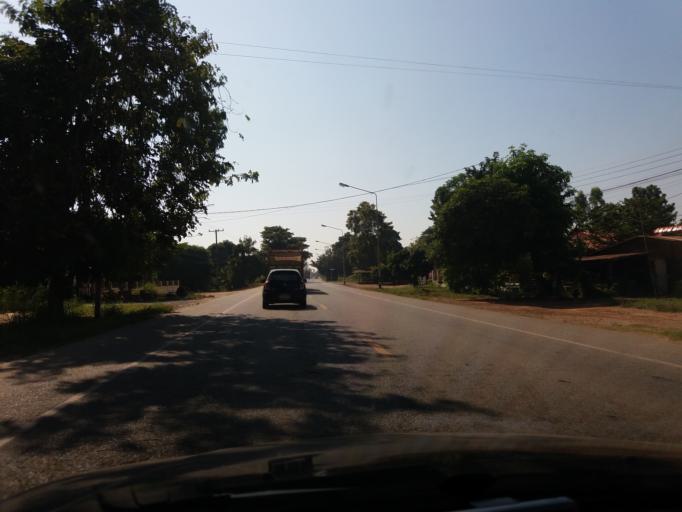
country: TH
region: Kamphaeng Phet
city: Khlong Khlung
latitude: 16.1664
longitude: 99.8010
